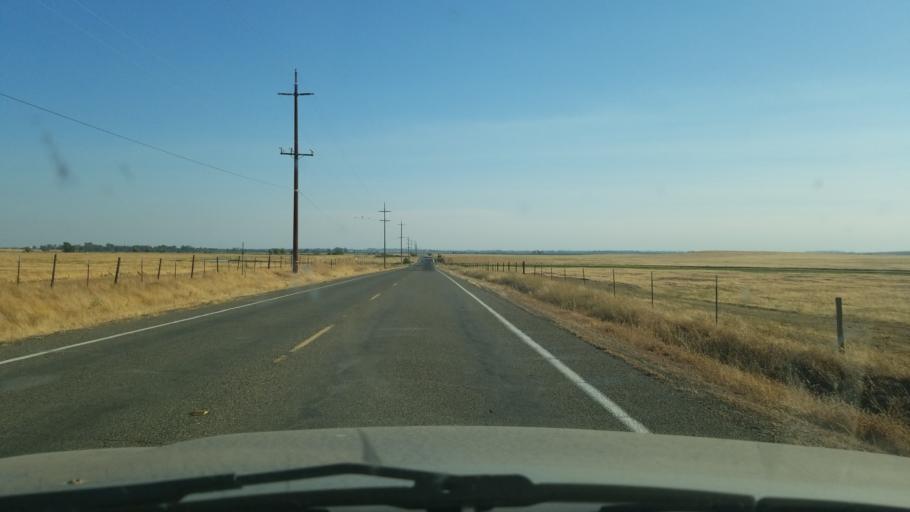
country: US
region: California
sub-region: Merced County
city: Merced
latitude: 37.4137
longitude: -120.4500
